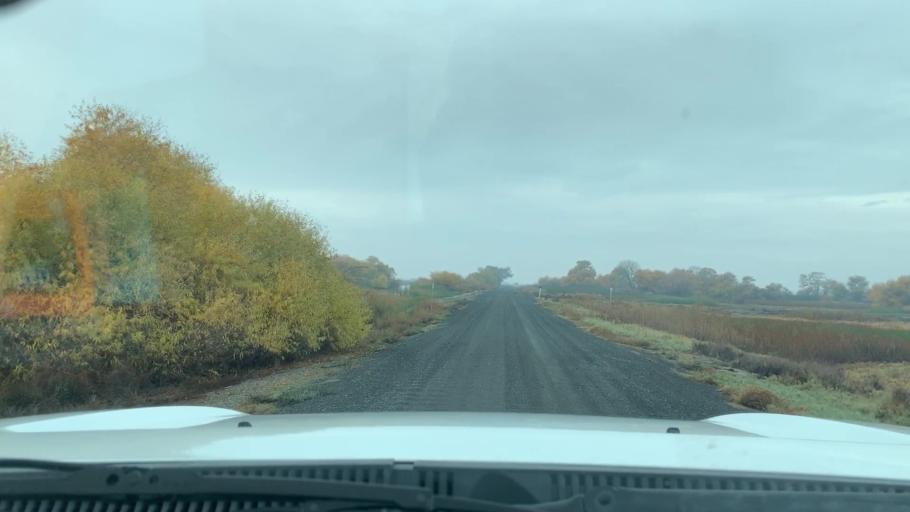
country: US
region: California
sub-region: Kern County
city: Lost Hills
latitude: 35.7336
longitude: -119.5992
